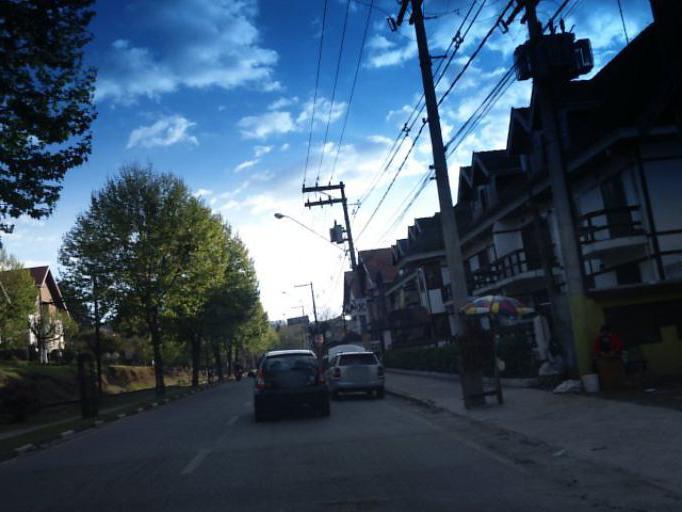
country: BR
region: Sao Paulo
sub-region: Campos Do Jordao
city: Campos do Jordao
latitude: -22.7250
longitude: -45.5783
